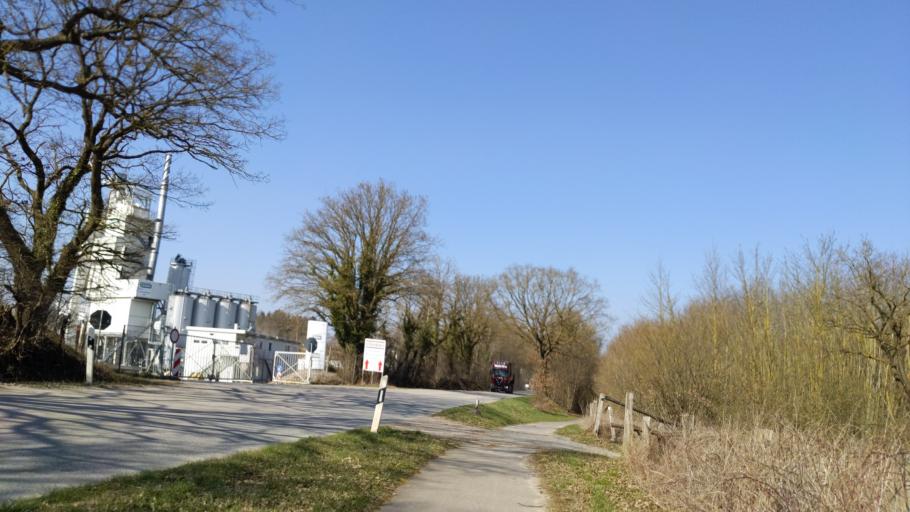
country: DE
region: Schleswig-Holstein
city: Susel
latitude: 54.0876
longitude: 10.7138
